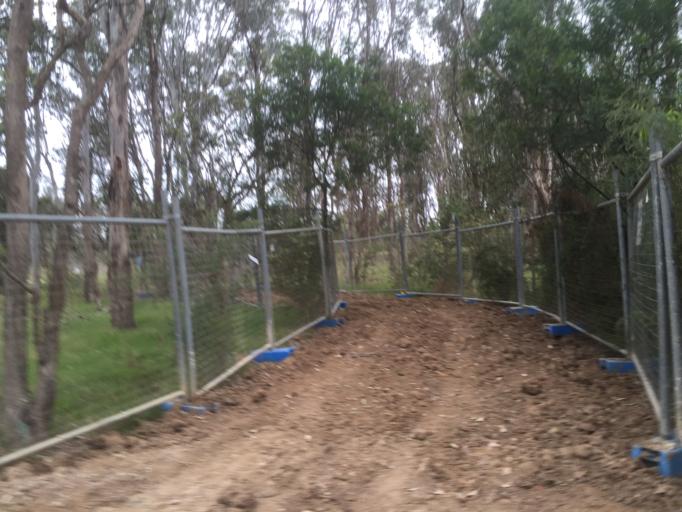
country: AU
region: New South Wales
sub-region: Blacktown
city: Doonside
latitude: -33.7877
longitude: 150.8698
